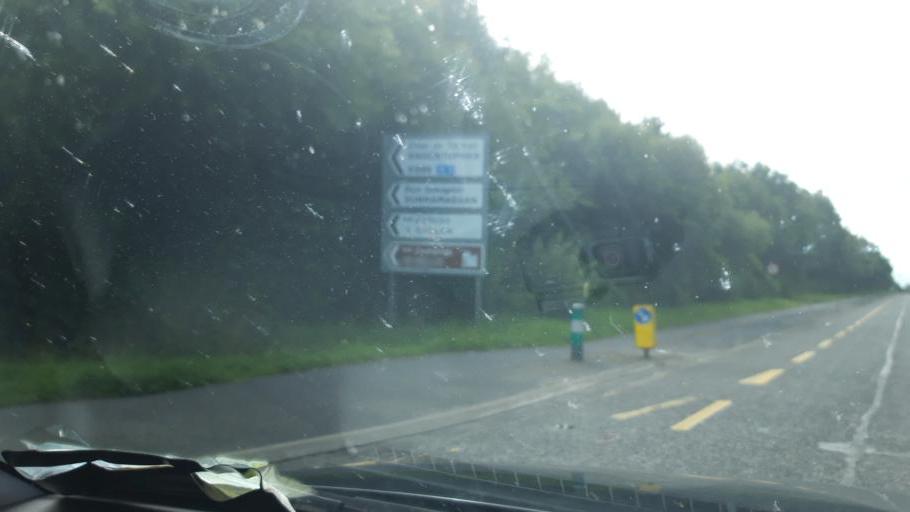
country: IE
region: Leinster
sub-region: Kilkenny
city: Callan
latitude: 52.5446
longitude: -7.3965
